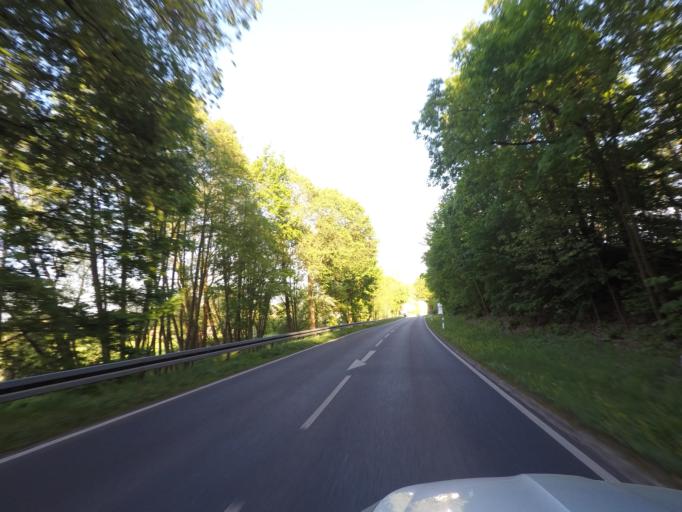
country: DE
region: Brandenburg
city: Bad Freienwalde
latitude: 52.7878
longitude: 14.0060
